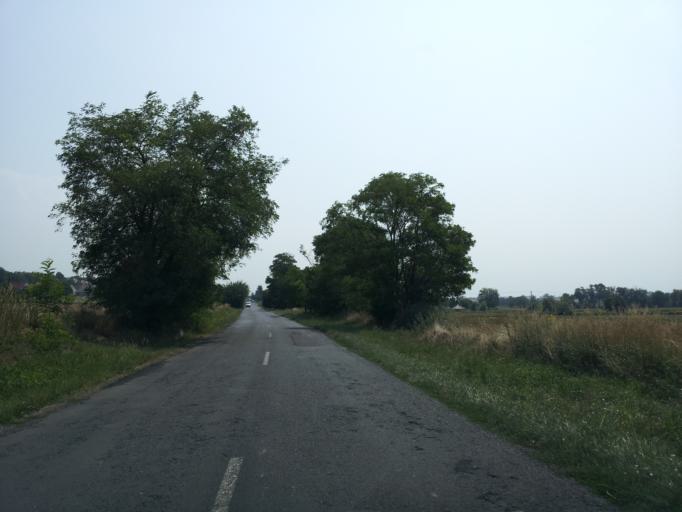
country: HU
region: Gyor-Moson-Sopron
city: Pannonhalma
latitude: 47.5082
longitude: 17.7785
